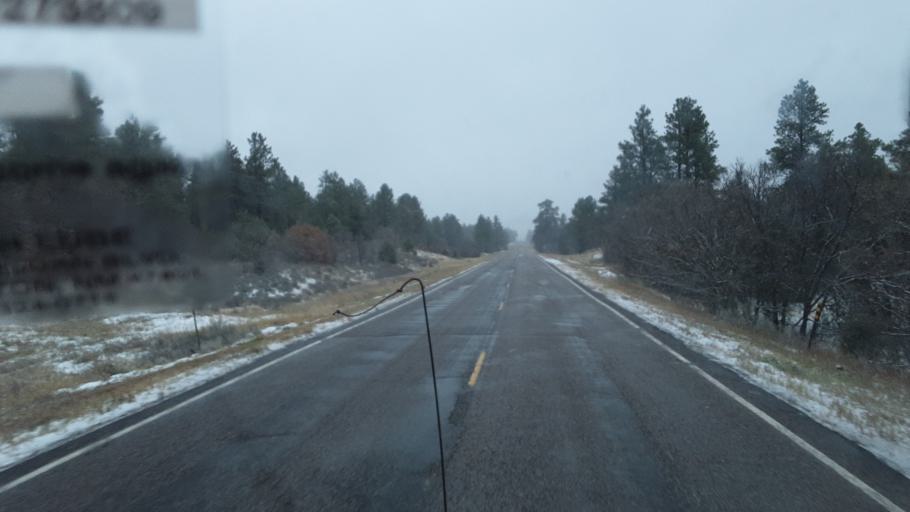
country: US
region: New Mexico
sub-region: Rio Arriba County
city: Tierra Amarilla
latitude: 36.6727
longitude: -106.5576
